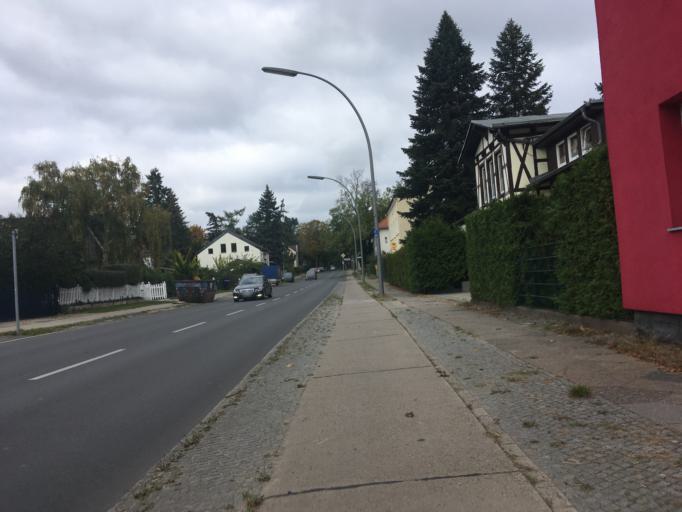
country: DE
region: Berlin
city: Gatow
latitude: 52.4908
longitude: 13.1804
